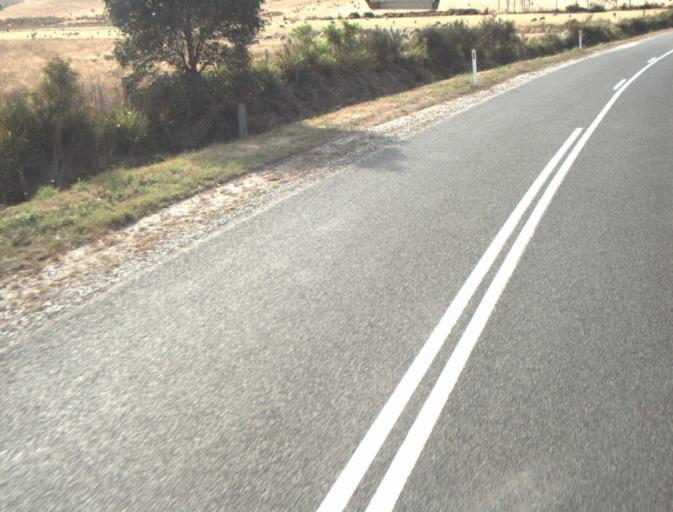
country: AU
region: Tasmania
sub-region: Launceston
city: Mayfield
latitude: -41.2239
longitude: 147.1219
